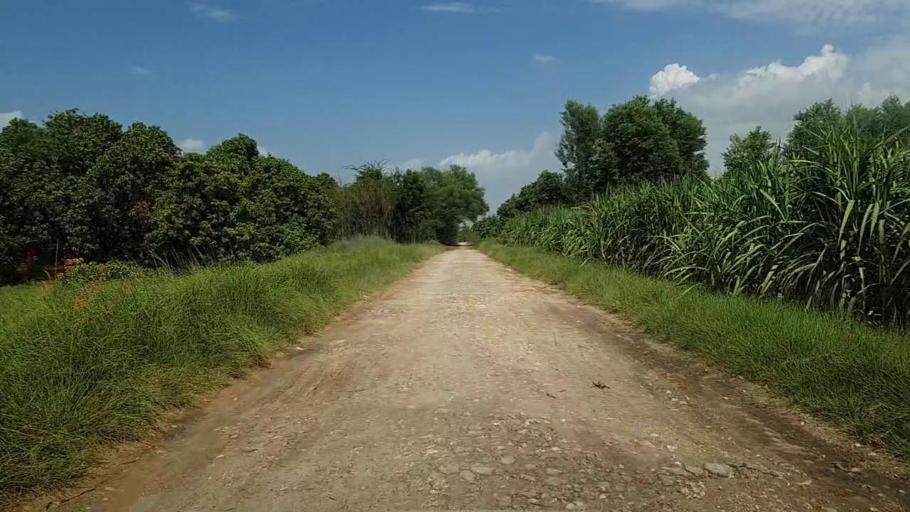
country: PK
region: Sindh
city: Bhiria
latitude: 26.9213
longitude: 68.2164
